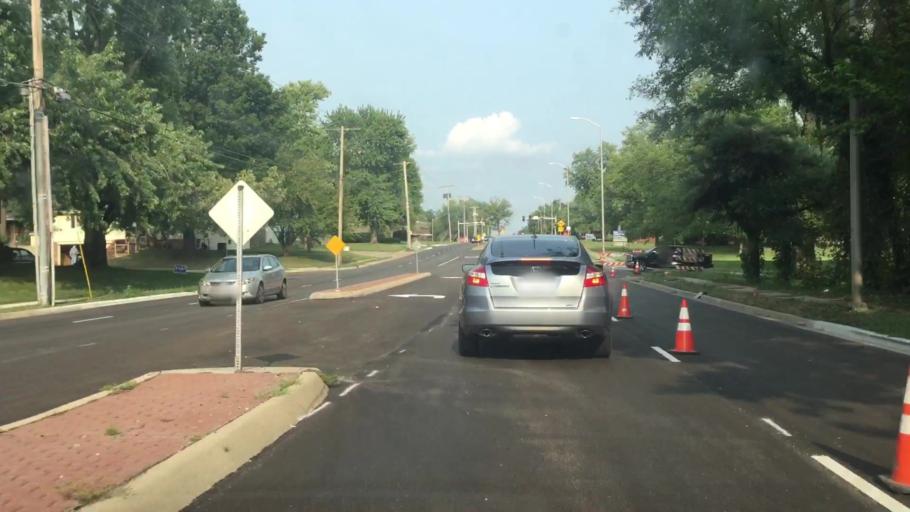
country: US
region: Kansas
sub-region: Johnson County
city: Lenexa
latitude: 38.9566
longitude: -94.6983
